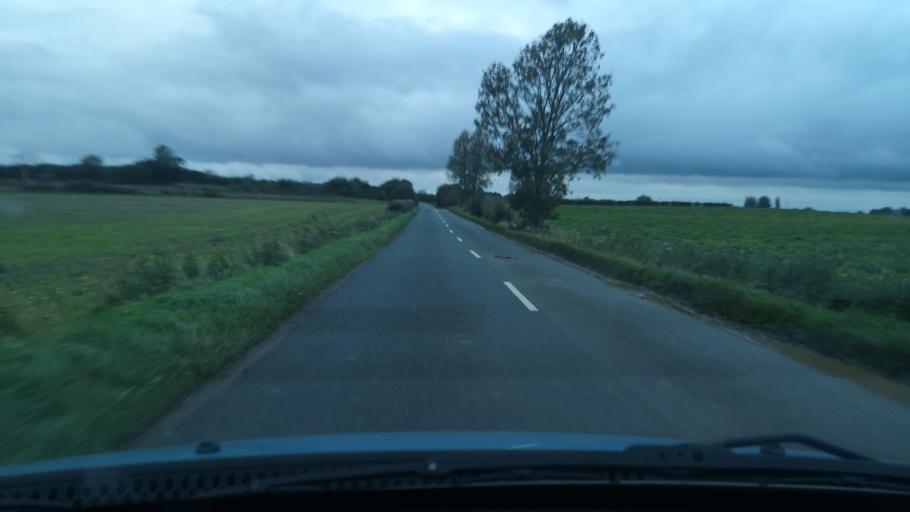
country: GB
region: England
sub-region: Doncaster
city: Norton
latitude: 53.6368
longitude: -1.2067
